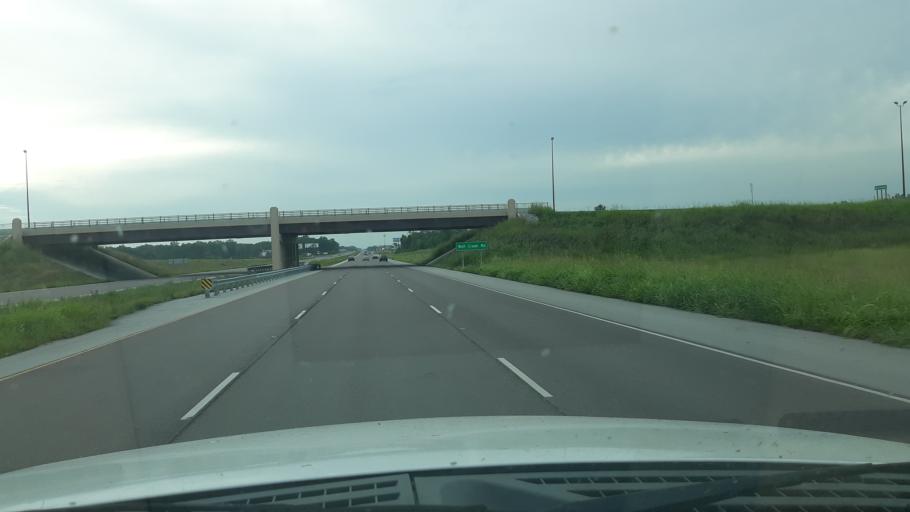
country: US
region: Illinois
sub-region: Williamson County
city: Crainville
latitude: 37.7452
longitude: -89.0568
